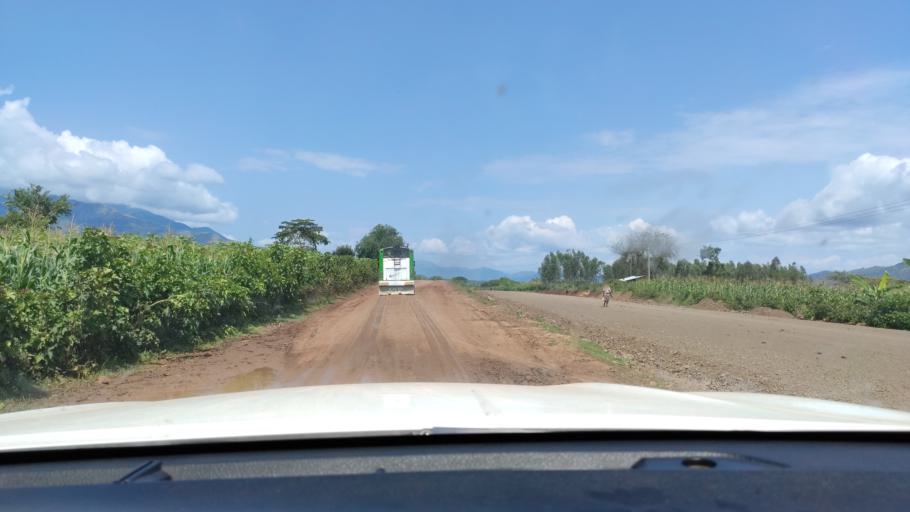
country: ET
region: Southern Nations, Nationalities, and People's Region
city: Felege Neway
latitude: 6.3673
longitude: 36.9930
